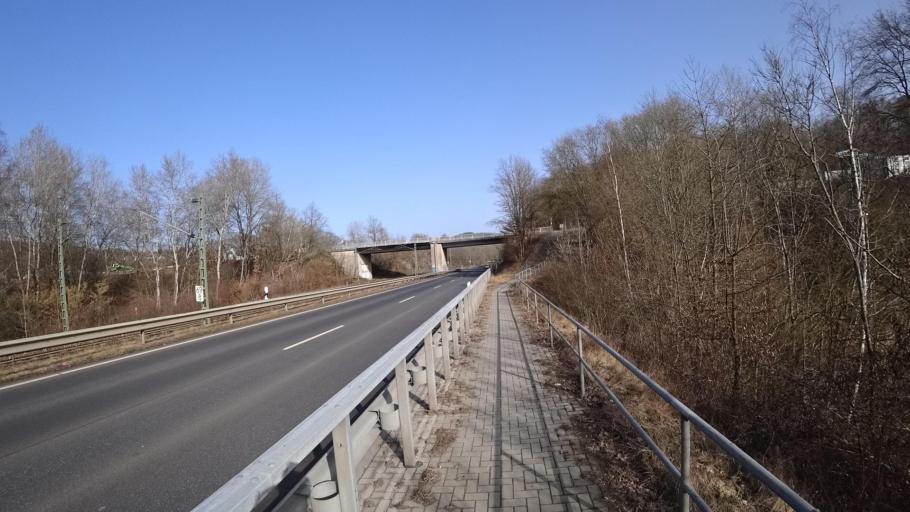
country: DE
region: Rheinland-Pfalz
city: Wissen
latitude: 50.7793
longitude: 7.7204
